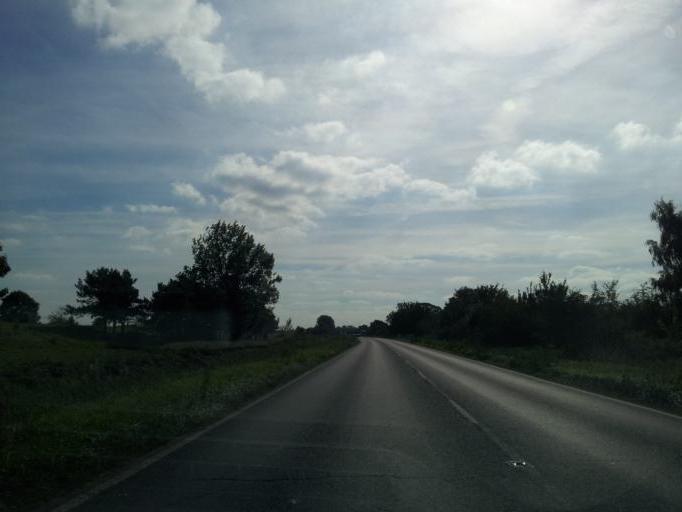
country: GB
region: England
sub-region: Cambridgeshire
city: Waterbeach
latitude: 52.2790
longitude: 0.1723
